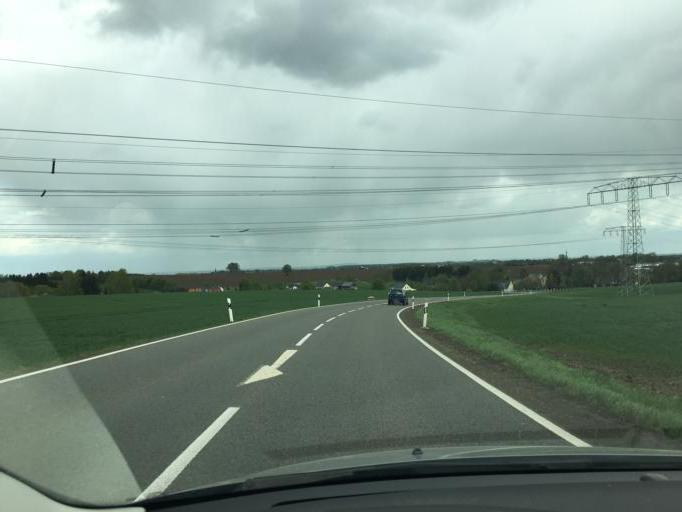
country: DE
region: Saxony
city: Limbach-Oberfrohna
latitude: 50.8249
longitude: 12.7548
